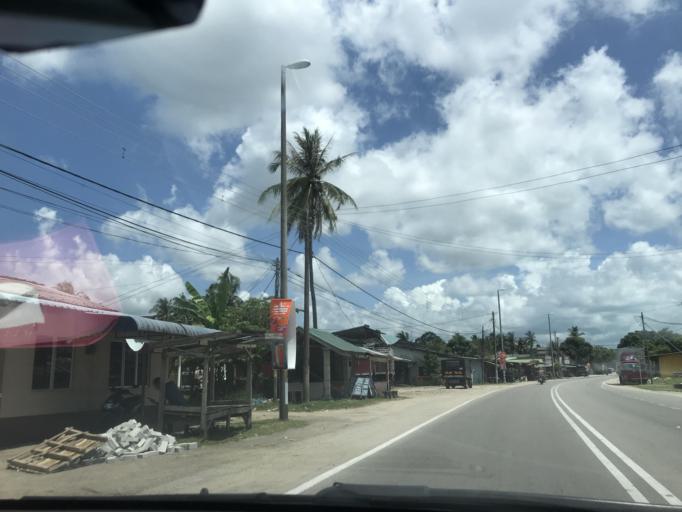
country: MY
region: Kelantan
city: Tumpat
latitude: 6.2196
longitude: 102.1129
